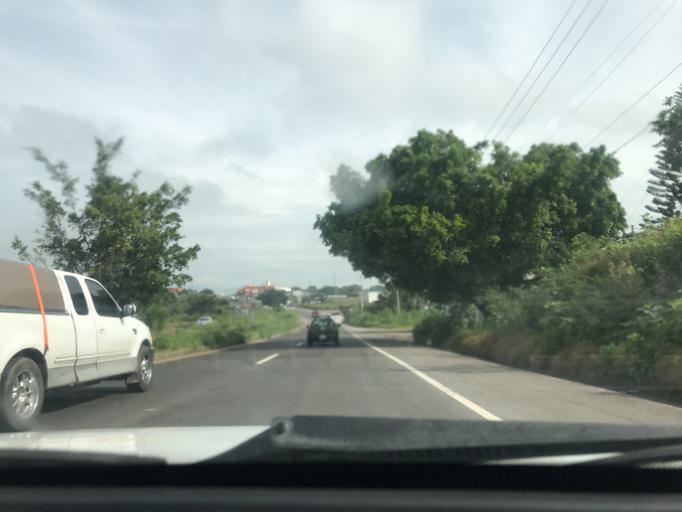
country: MX
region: Morelos
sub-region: Yecapixtla
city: Juan Morales
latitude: 18.8061
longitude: -98.9153
